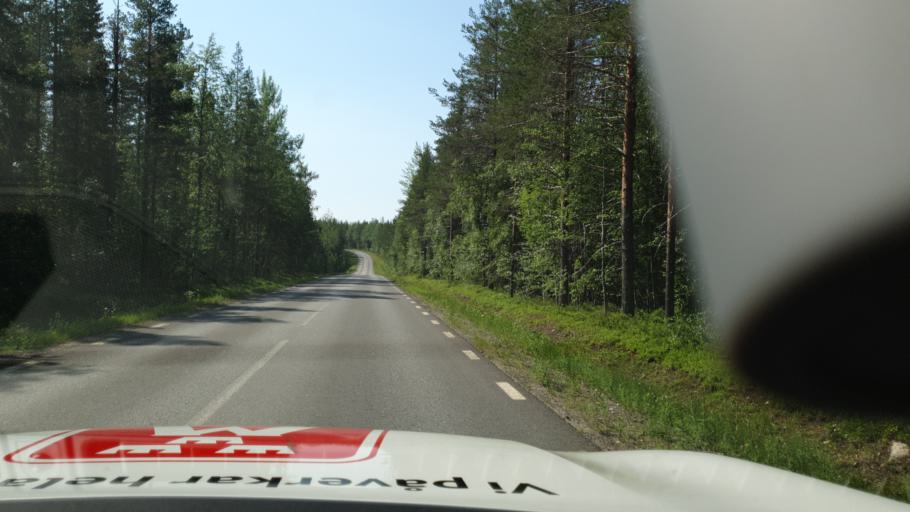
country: SE
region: Vaesterbotten
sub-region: Skelleftea Kommun
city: Langsele
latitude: 64.9701
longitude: 20.0473
